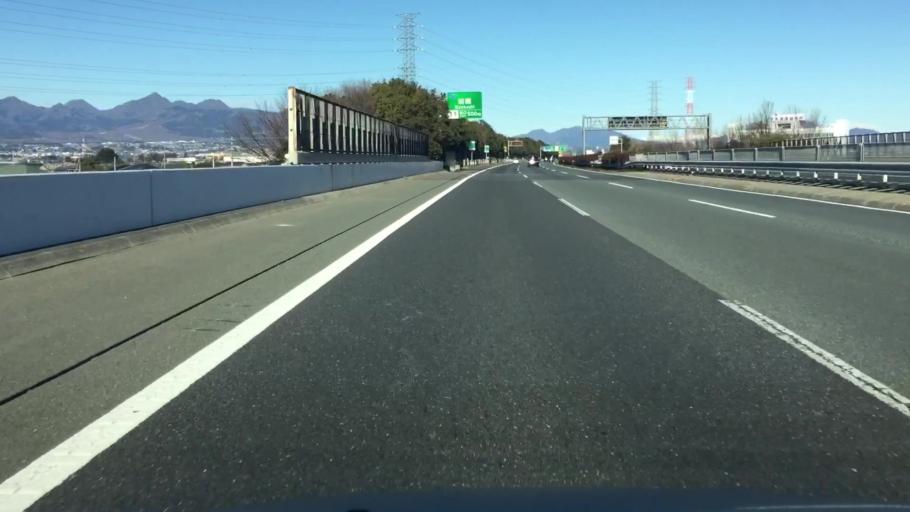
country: JP
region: Gunma
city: Takasaki
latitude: 36.3666
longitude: 139.0310
